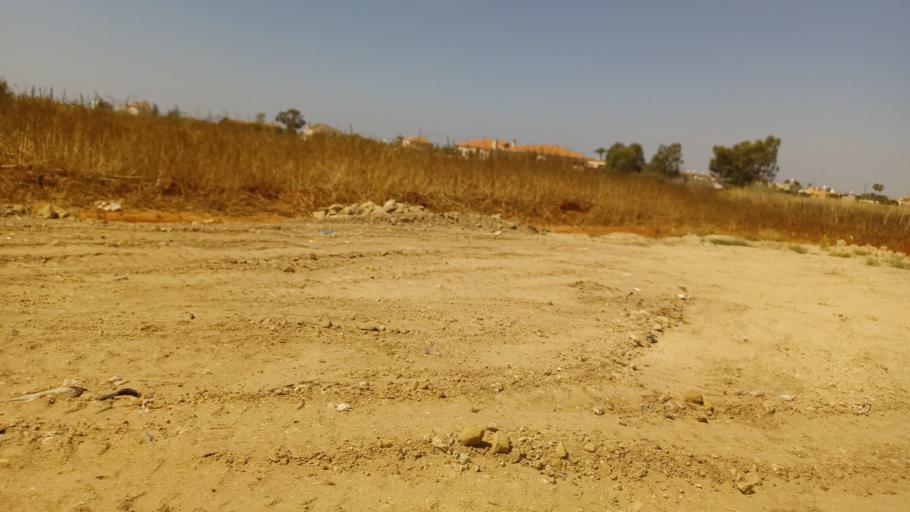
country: CY
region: Ammochostos
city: Liopetri
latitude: 35.0127
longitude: 33.8885
